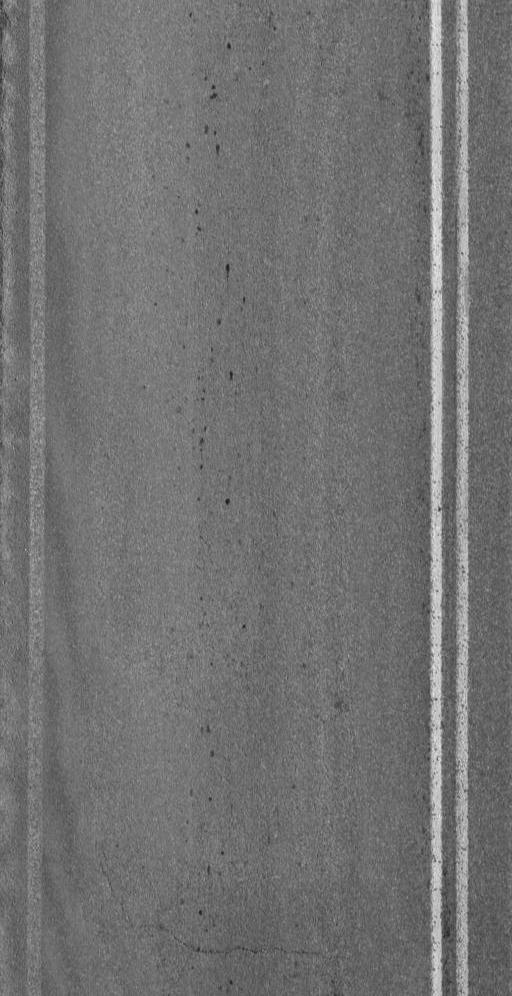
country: US
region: Vermont
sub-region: Washington County
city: Barre
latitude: 44.2737
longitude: -72.4915
